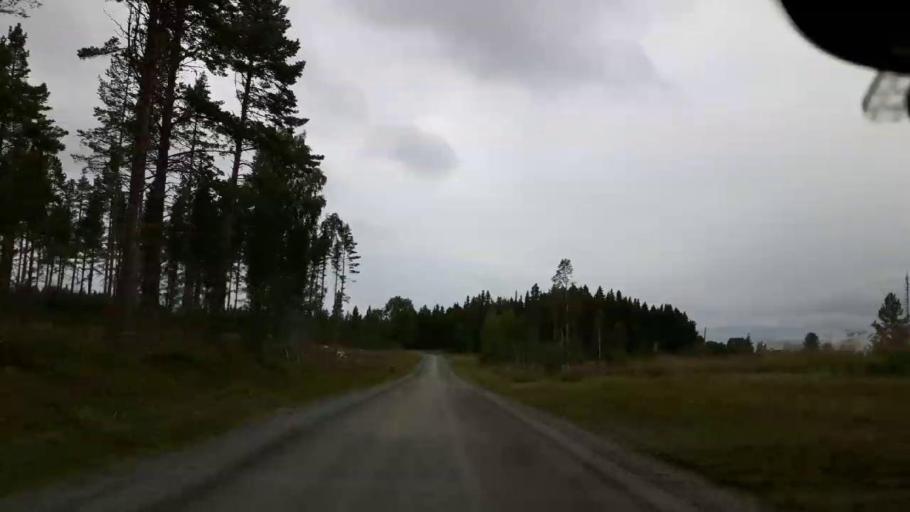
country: SE
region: Jaemtland
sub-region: OEstersunds Kommun
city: Ostersund
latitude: 63.1149
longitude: 14.5439
